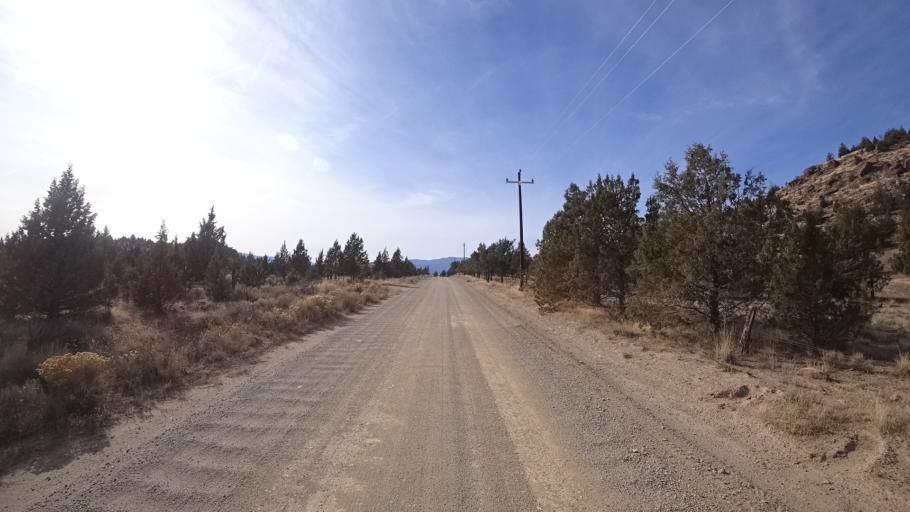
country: US
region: California
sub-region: Siskiyou County
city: Montague
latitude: 41.5799
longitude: -122.4575
